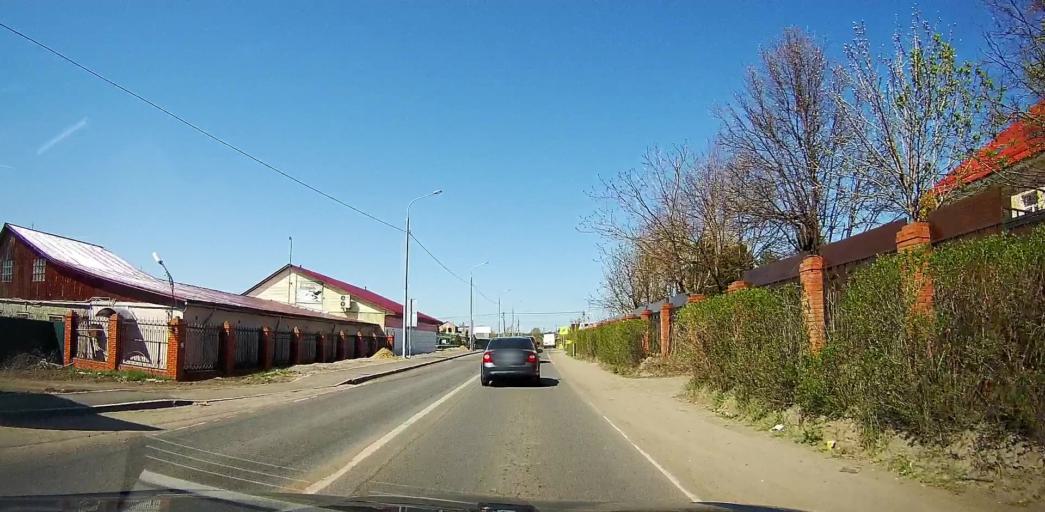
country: RU
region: Moskovskaya
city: Beloozerskiy
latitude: 55.4724
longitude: 38.4125
